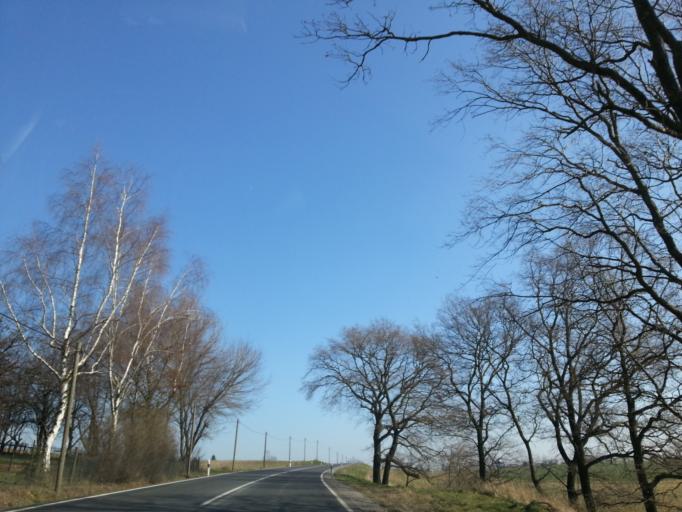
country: DE
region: Saxony
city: Halsbrucke
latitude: 50.9214
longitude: 13.3818
